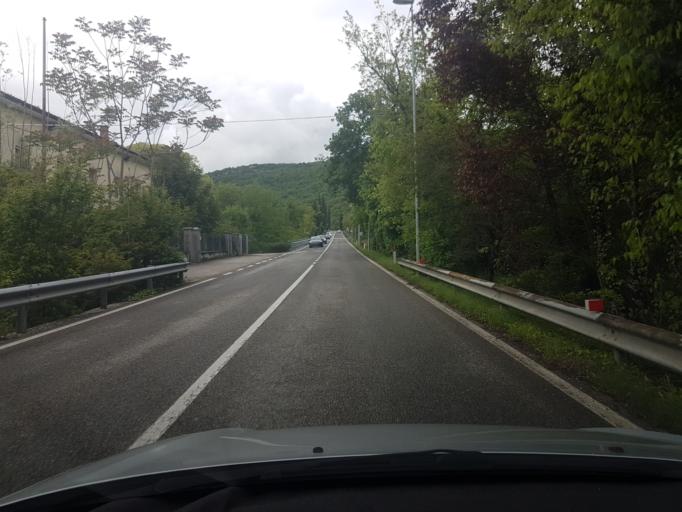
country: IT
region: Friuli Venezia Giulia
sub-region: Provincia di Gorizia
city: Doberdo del Lago
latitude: 45.8235
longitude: 13.5786
